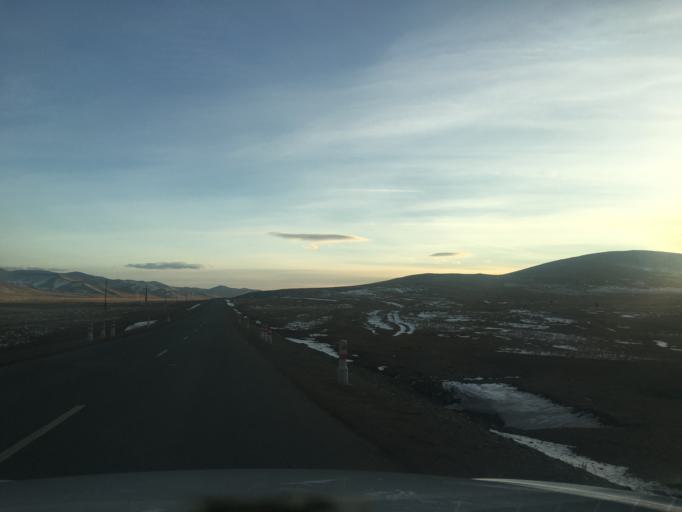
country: MN
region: Central Aimak
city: Mandal
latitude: 48.1849
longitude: 106.7040
